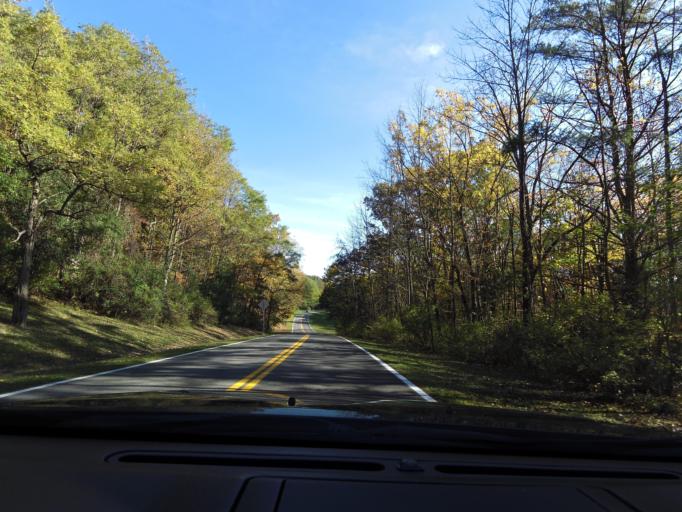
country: US
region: New York
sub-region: Wyoming County
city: Castile
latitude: 42.6383
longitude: -77.9877
